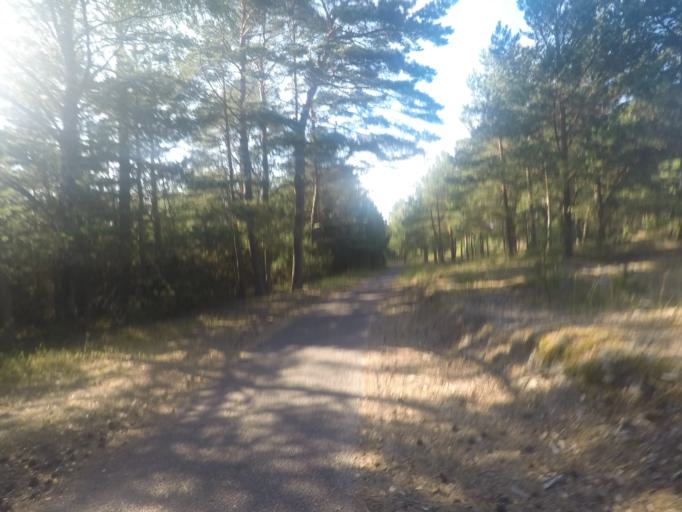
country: LT
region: Klaipedos apskritis
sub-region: Klaipeda
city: Klaipeda
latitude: 55.6074
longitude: 21.1168
